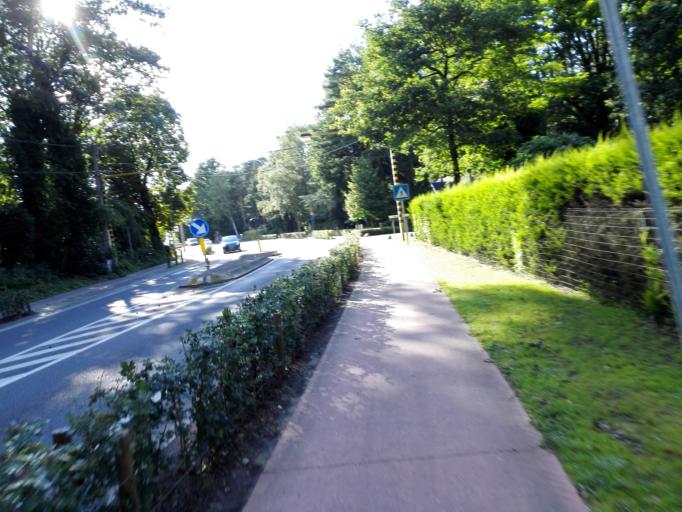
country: BE
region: Flanders
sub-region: Provincie Antwerpen
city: Bonheiden
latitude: 51.0173
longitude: 4.5765
